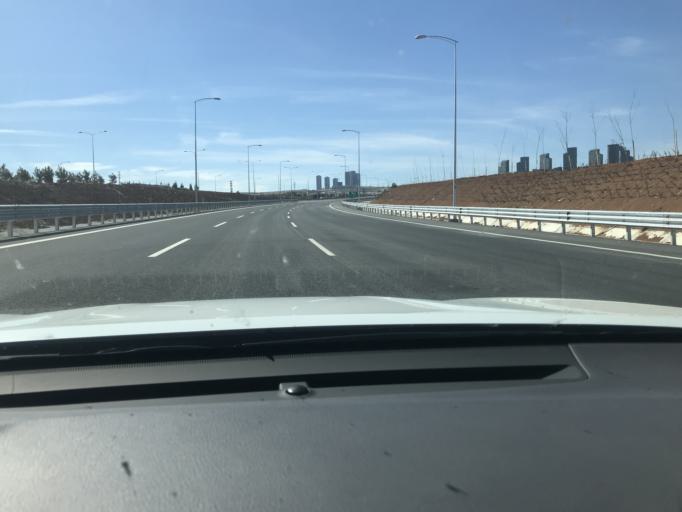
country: TR
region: Ankara
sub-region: Goelbasi
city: Golbasi
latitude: 39.7884
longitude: 32.7390
